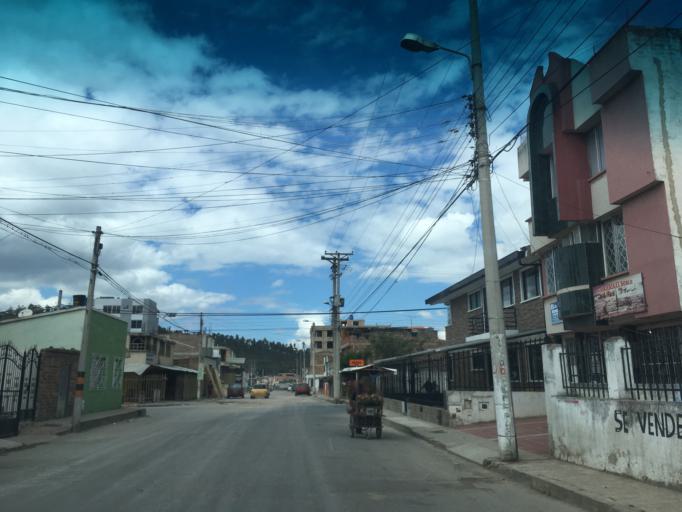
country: CO
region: Boyaca
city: Sogamoso
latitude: 5.7205
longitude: -72.9410
